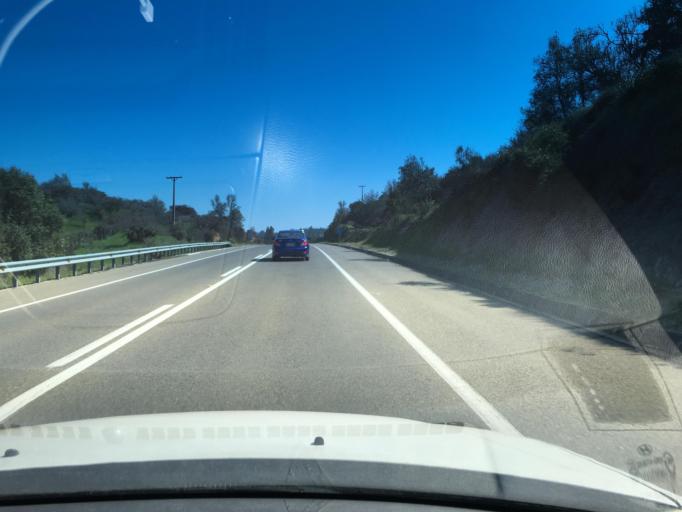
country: CL
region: Valparaiso
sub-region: San Antonio Province
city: El Tabo
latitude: -33.3885
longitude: -71.4655
